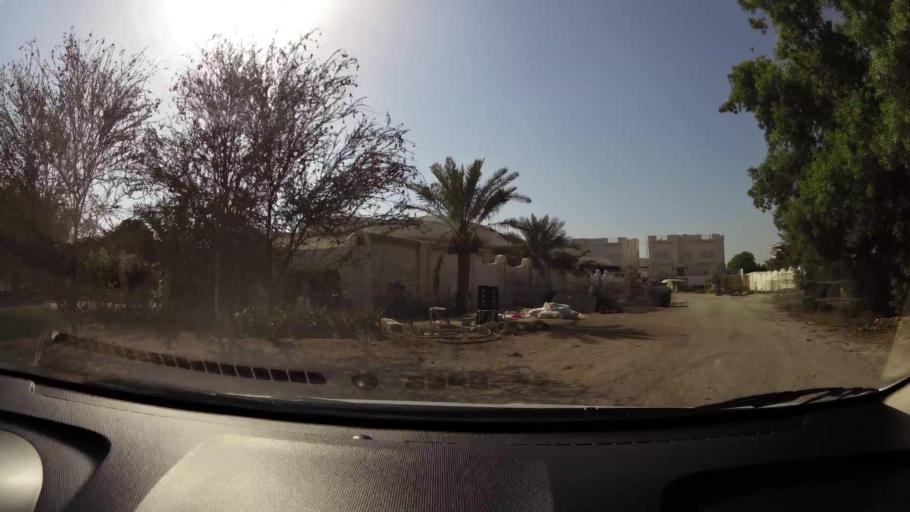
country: AE
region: Ajman
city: Ajman
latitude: 25.4183
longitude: 55.4634
